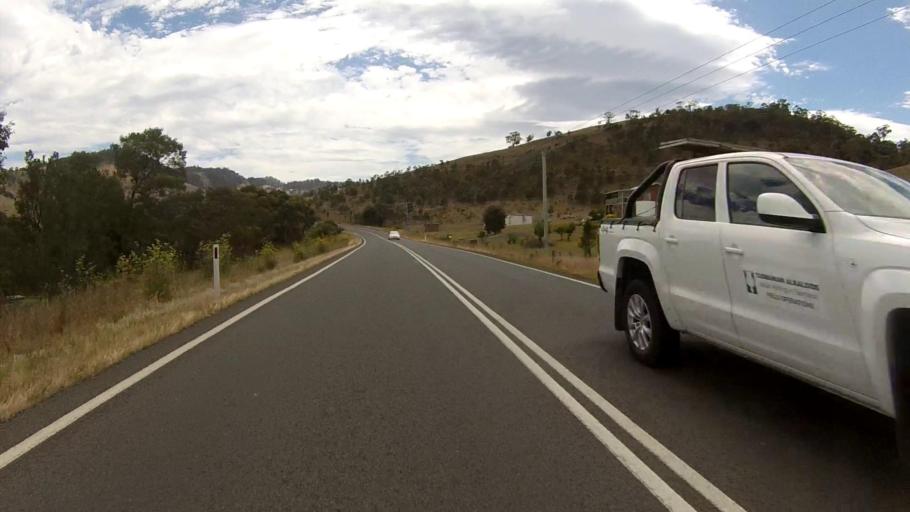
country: AU
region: Tasmania
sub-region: Brighton
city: Old Beach
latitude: -42.6848
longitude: 147.3534
